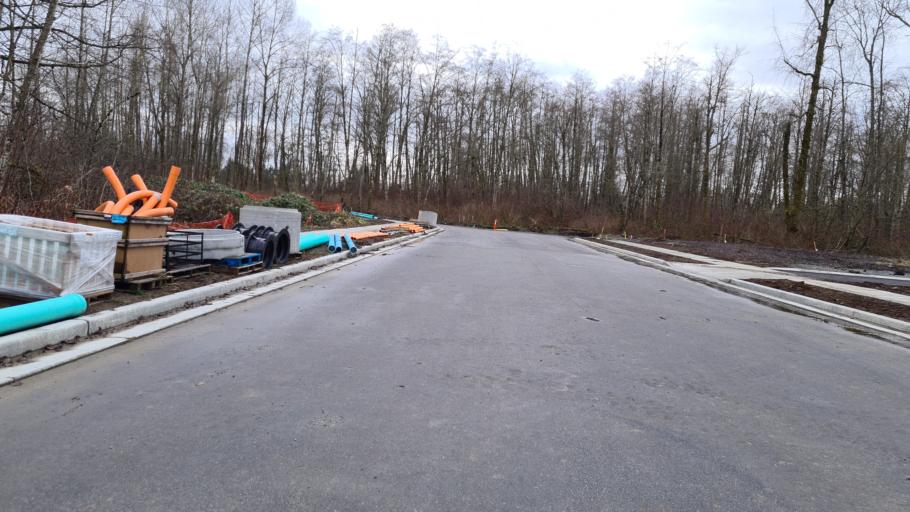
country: CA
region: British Columbia
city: Walnut Grove
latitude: 49.1415
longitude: -122.6485
